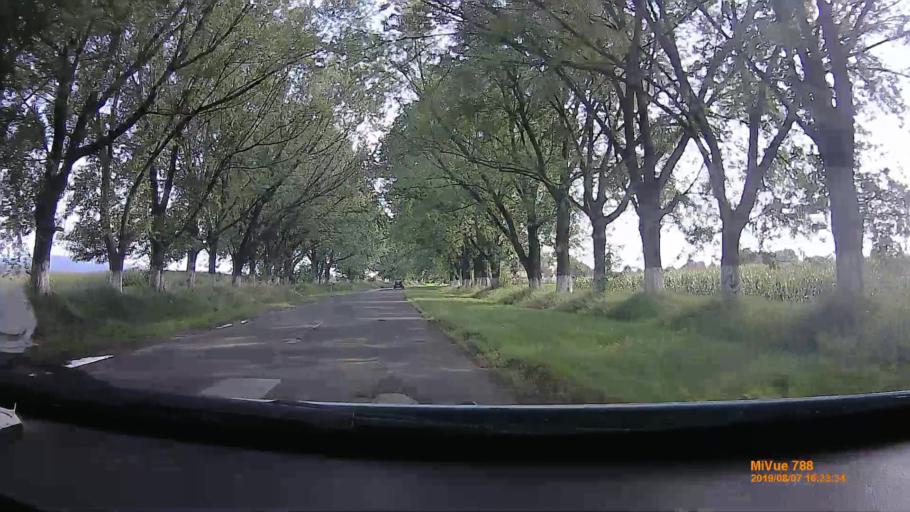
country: HU
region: Borsod-Abauj-Zemplen
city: Gonc
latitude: 48.4270
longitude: 21.2374
